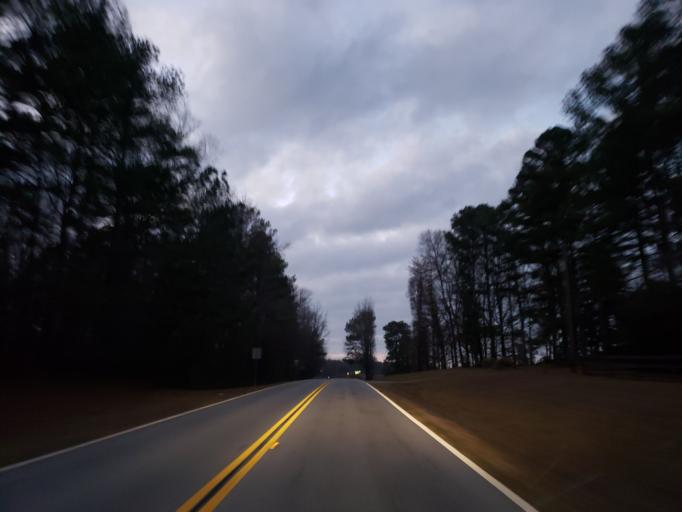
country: US
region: Georgia
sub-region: Carroll County
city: Temple
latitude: 33.7661
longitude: -85.0482
